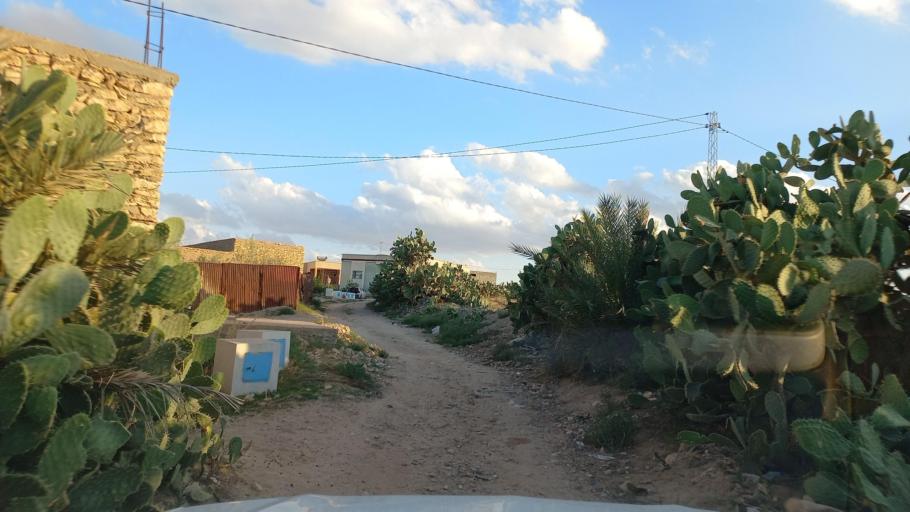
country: TN
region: Al Qasrayn
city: Sbiba
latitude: 35.3791
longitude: 9.0509
